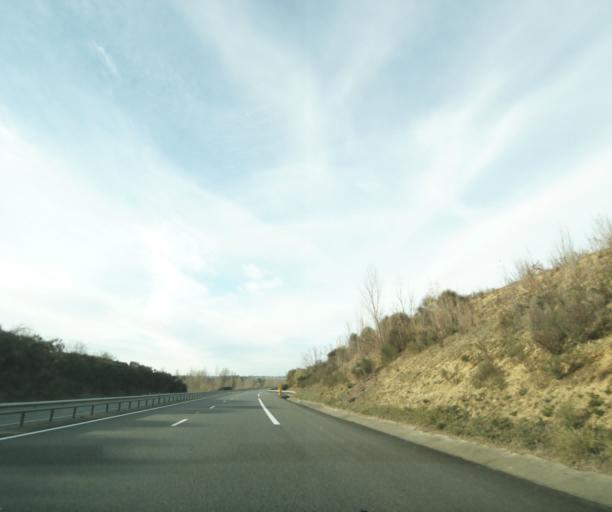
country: FR
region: Midi-Pyrenees
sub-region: Departement du Gers
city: Aubiet
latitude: 43.6428
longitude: 0.8073
